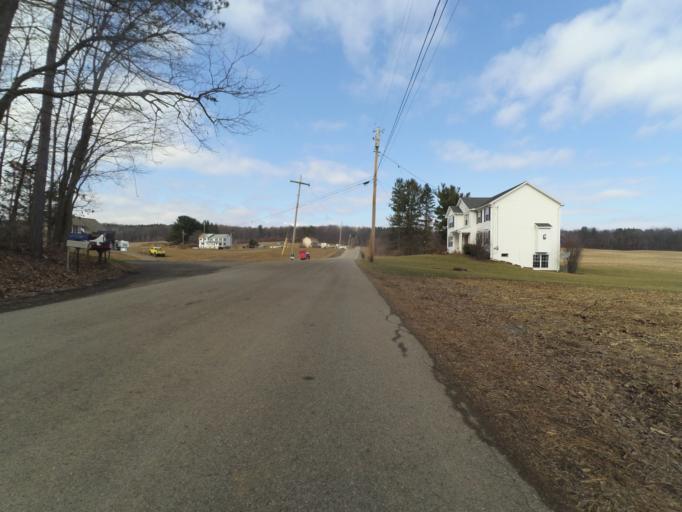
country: US
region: Pennsylvania
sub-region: Centre County
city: Park Forest Village
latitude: 40.7751
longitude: -77.9237
